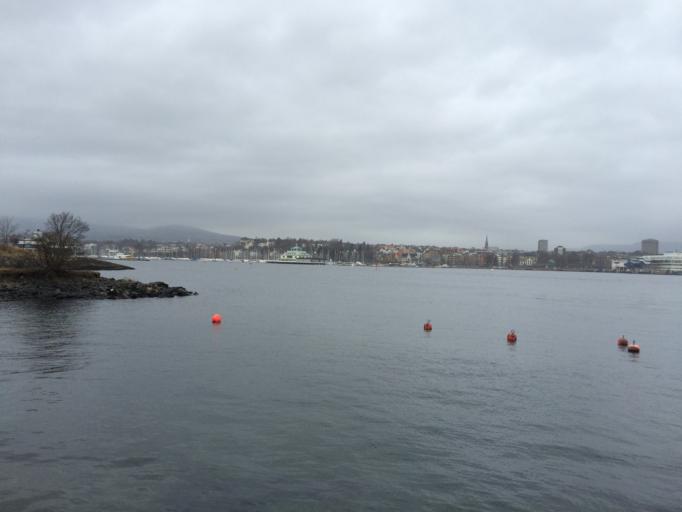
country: NO
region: Oslo
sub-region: Oslo
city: Sjolyststranda
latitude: 59.9038
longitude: 10.6998
